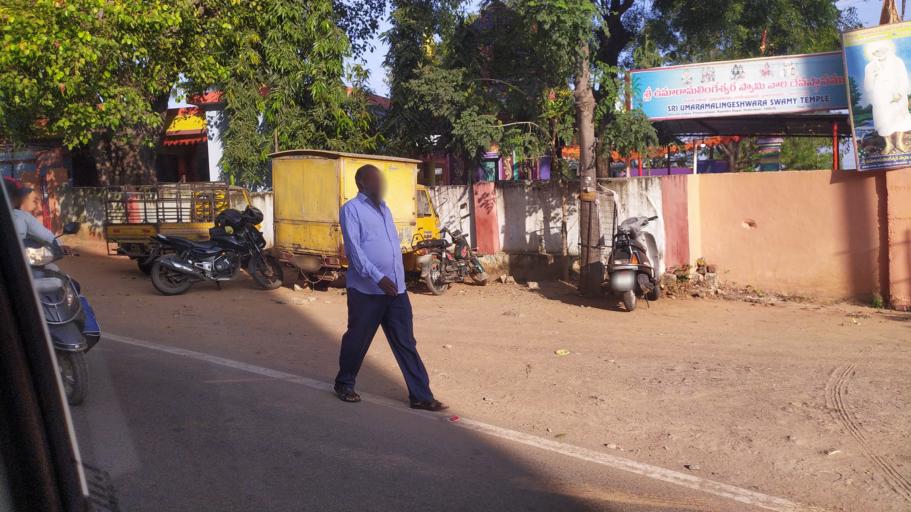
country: IN
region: Telangana
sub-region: Hyderabad
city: Hyderabad
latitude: 17.3272
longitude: 78.4216
